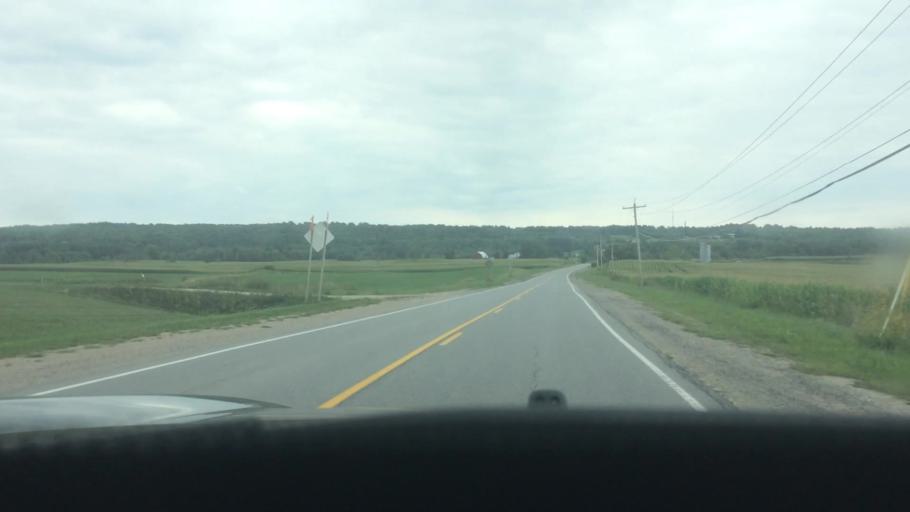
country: US
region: New York
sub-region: St. Lawrence County
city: Canton
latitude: 44.5544
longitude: -75.1108
